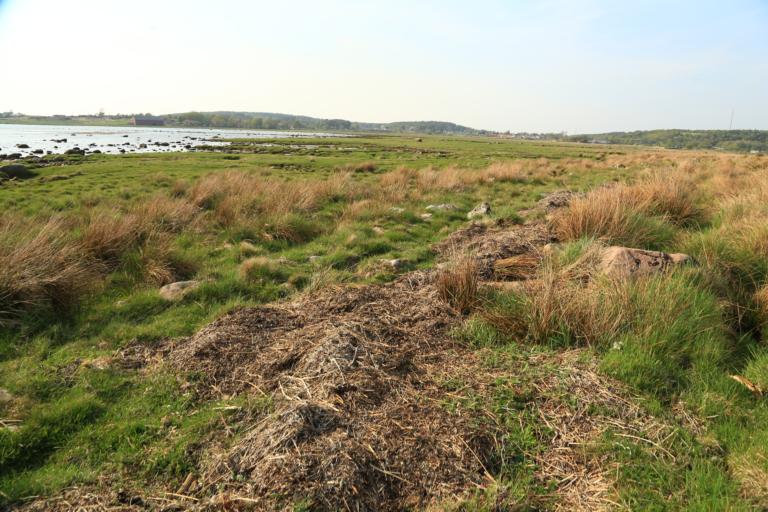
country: SE
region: Halland
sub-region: Varbergs Kommun
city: Varberg
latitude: 57.1597
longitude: 12.2288
